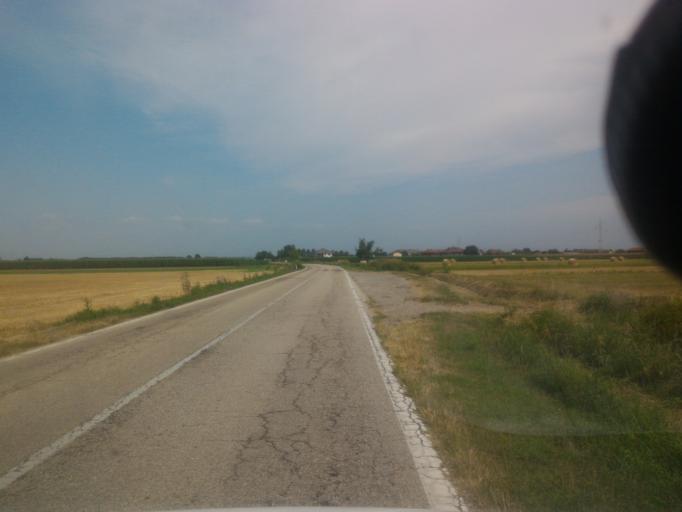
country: IT
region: Piedmont
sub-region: Provincia di Torino
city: Buriasco
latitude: 44.8590
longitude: 7.4301
